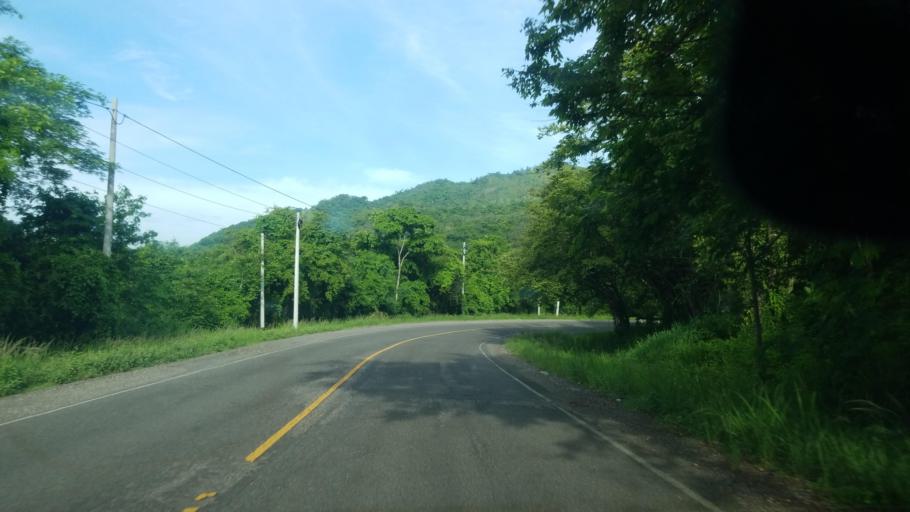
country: HN
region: Santa Barbara
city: Trinidad
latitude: 15.1347
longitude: -88.2521
